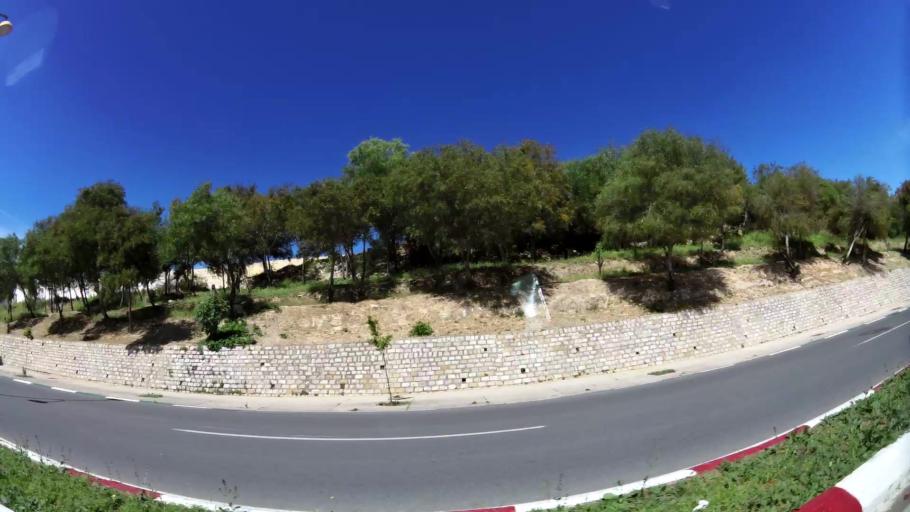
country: MA
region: Meknes-Tafilalet
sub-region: Meknes
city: Meknes
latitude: 33.8898
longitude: -5.5529
